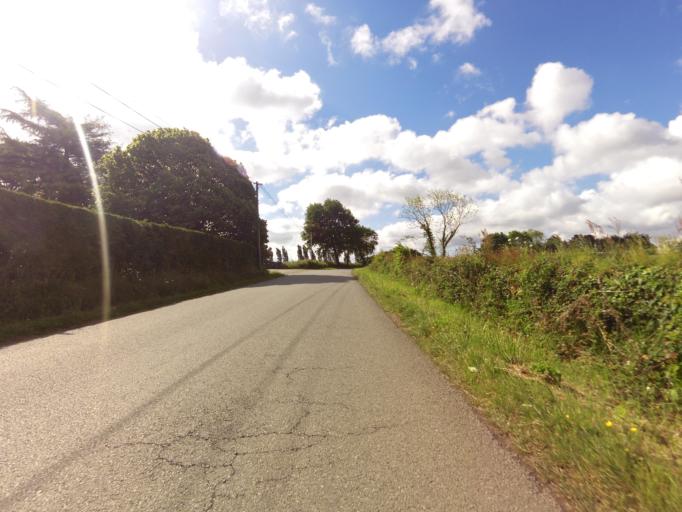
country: FR
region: Brittany
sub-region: Departement du Morbihan
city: Baden
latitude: 47.6288
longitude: -2.8965
